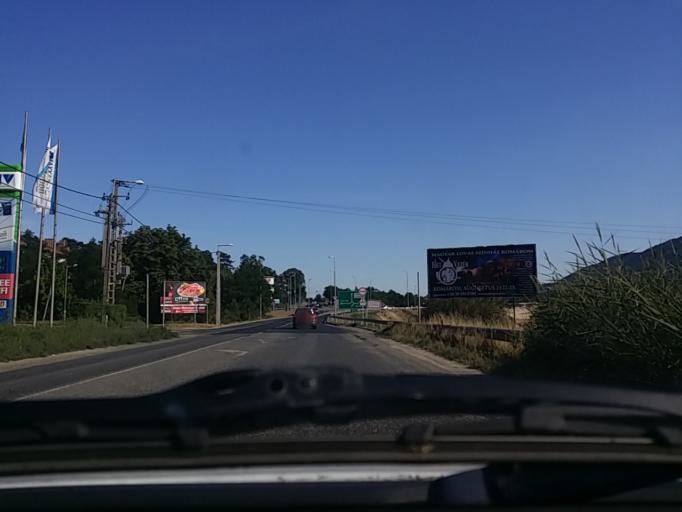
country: HU
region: Pest
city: Urom
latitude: 47.5851
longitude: 18.9979
